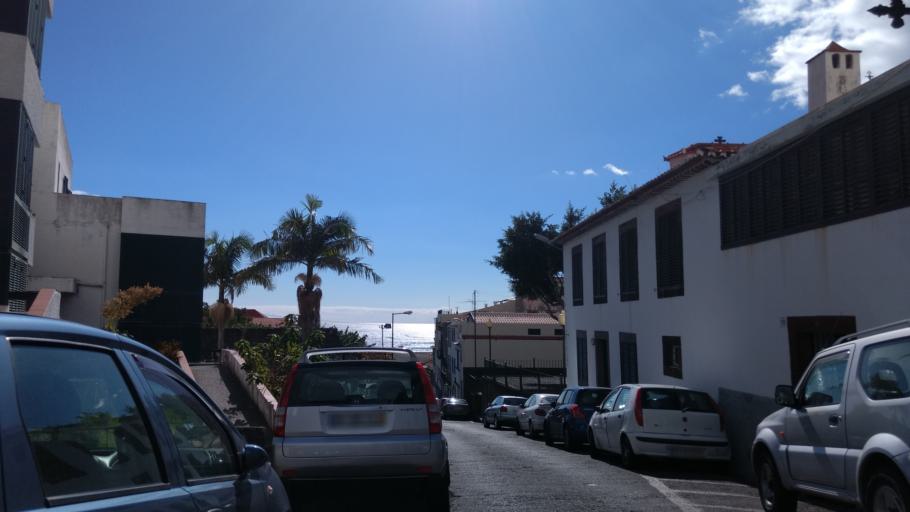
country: PT
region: Madeira
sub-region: Funchal
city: Nossa Senhora do Monte
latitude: 32.6546
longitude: -16.9084
